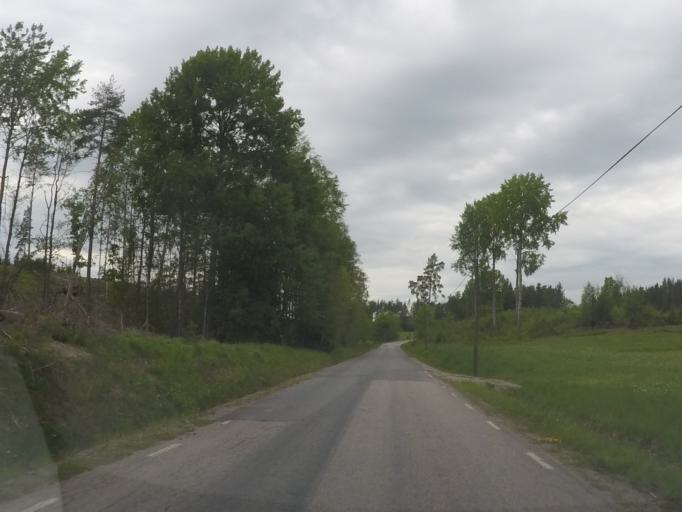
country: SE
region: Soedermanland
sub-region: Nykopings Kommun
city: Stigtomta
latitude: 58.8998
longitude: 16.8867
